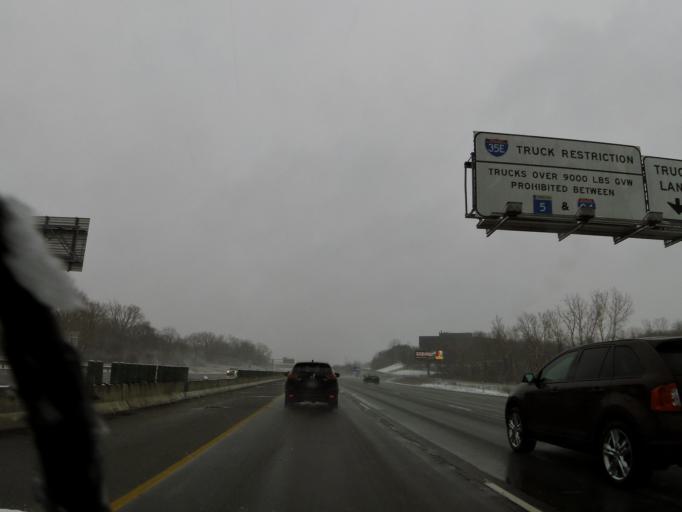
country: US
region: Minnesota
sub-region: Dakota County
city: Mendota Heights
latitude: 44.8611
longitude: -93.1743
